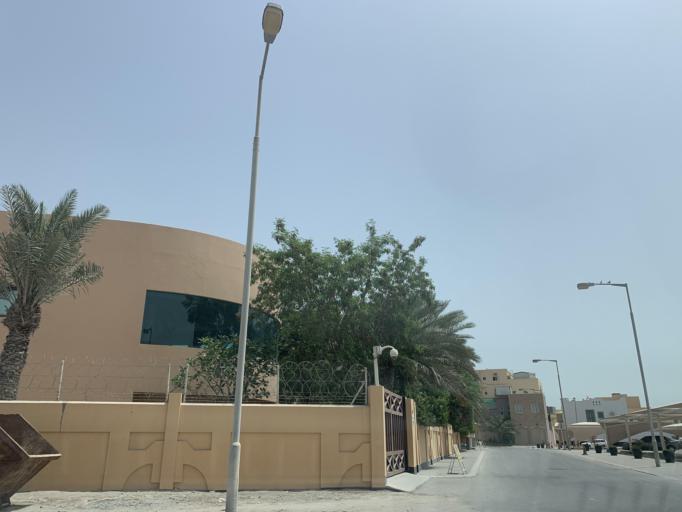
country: BH
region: Northern
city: Sitrah
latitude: 26.1451
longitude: 50.6003
